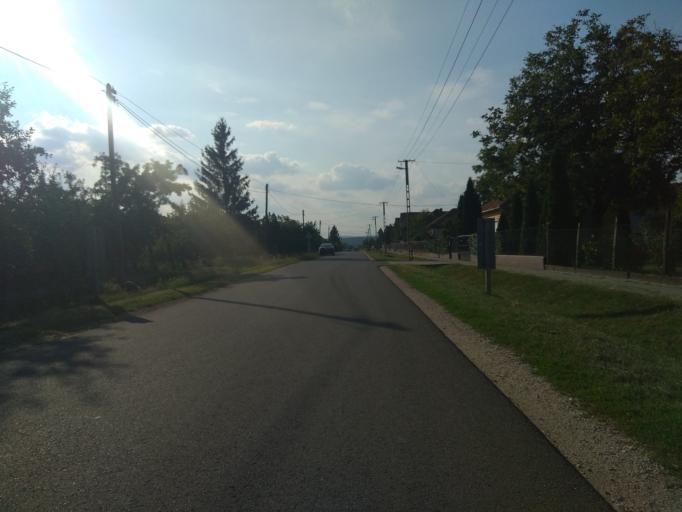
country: HU
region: Borsod-Abauj-Zemplen
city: Emod
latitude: 47.8912
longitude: 20.7627
